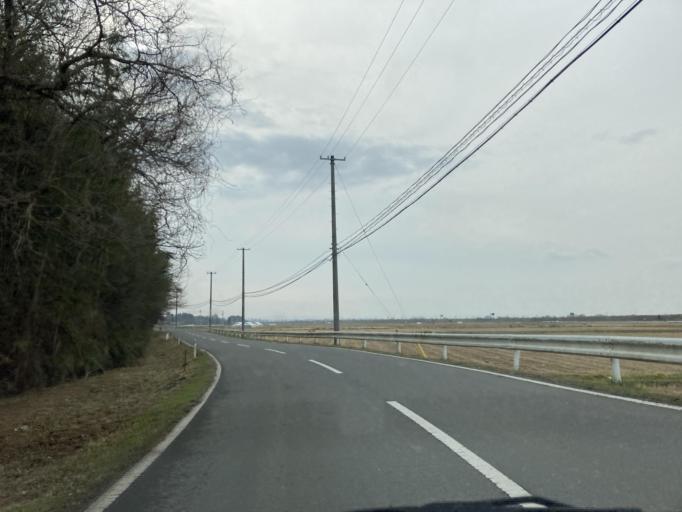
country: JP
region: Miyagi
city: Wakuya
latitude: 38.6865
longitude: 141.2754
